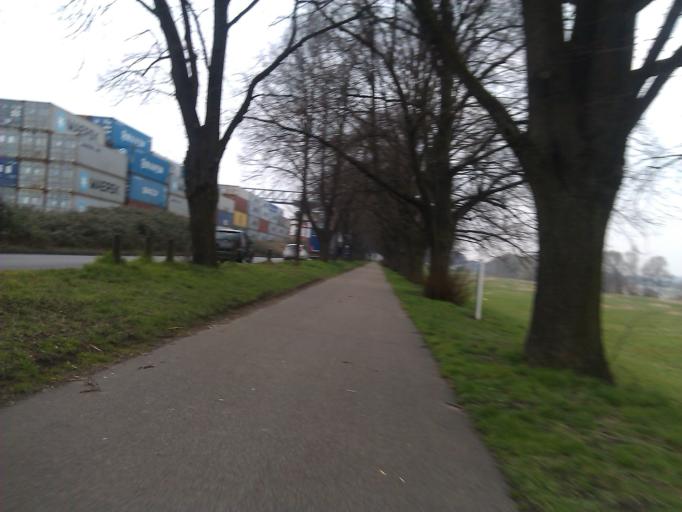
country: DE
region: North Rhine-Westphalia
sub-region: Regierungsbezirk Koln
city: Riehl
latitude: 50.9807
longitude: 6.9808
